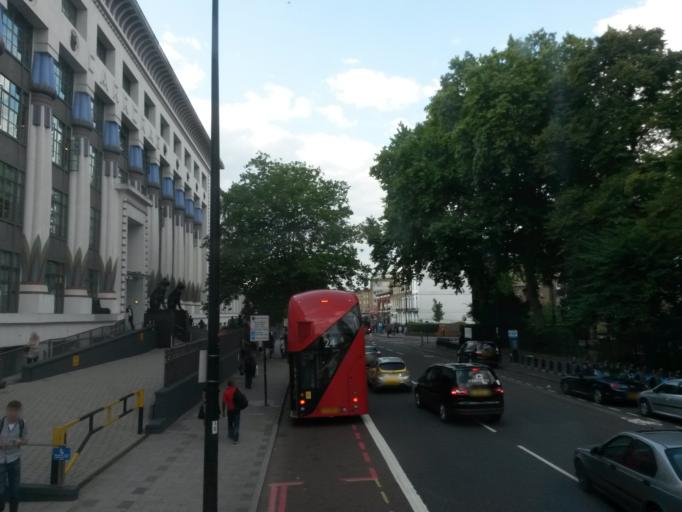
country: GB
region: England
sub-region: Greater London
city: Camden Town
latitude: 51.5331
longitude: -0.1393
